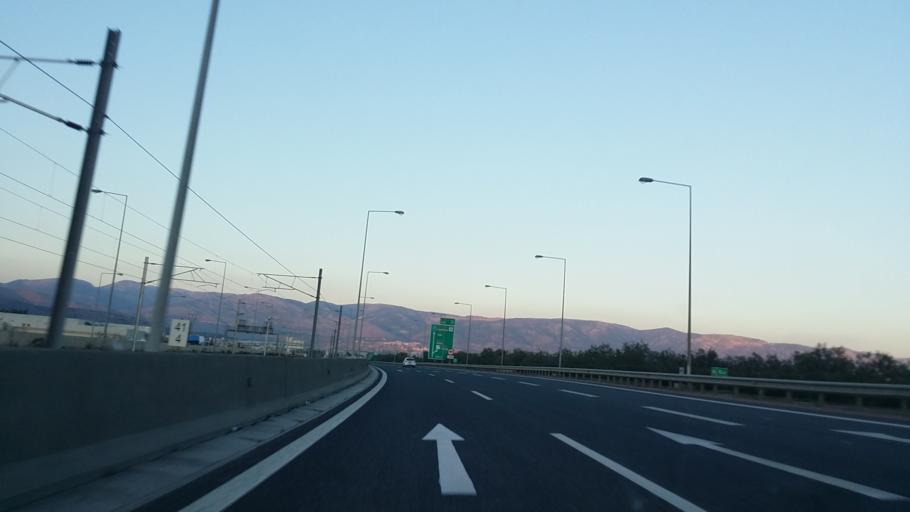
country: GR
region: Attica
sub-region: Nomarchia Dytikis Attikis
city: Magoula
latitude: 38.0625
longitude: 23.5210
